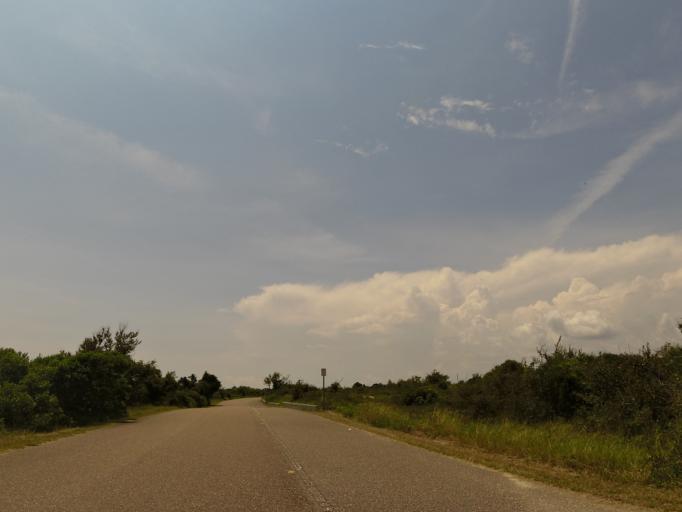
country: US
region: Florida
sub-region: Duval County
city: Atlantic Beach
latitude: 30.4408
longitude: -81.4141
